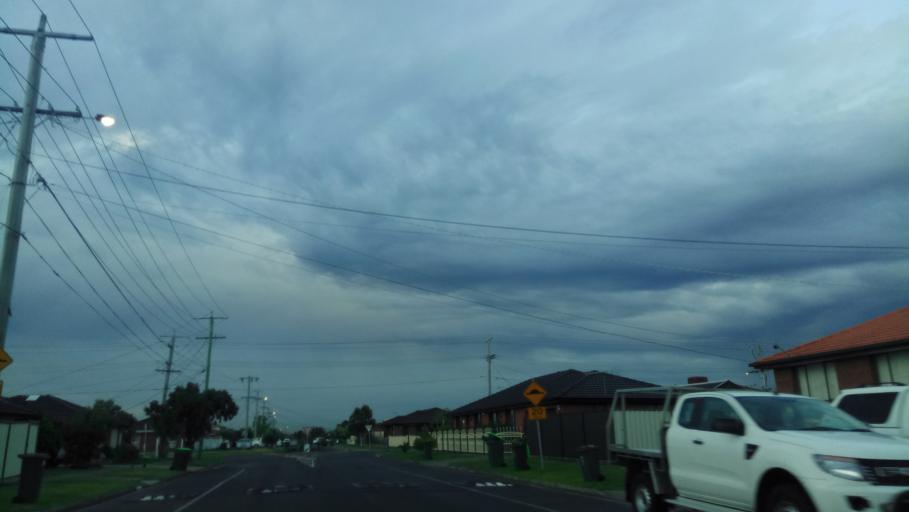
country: AU
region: Victoria
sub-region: Hobsons Bay
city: Laverton
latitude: -37.8732
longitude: 144.7728
